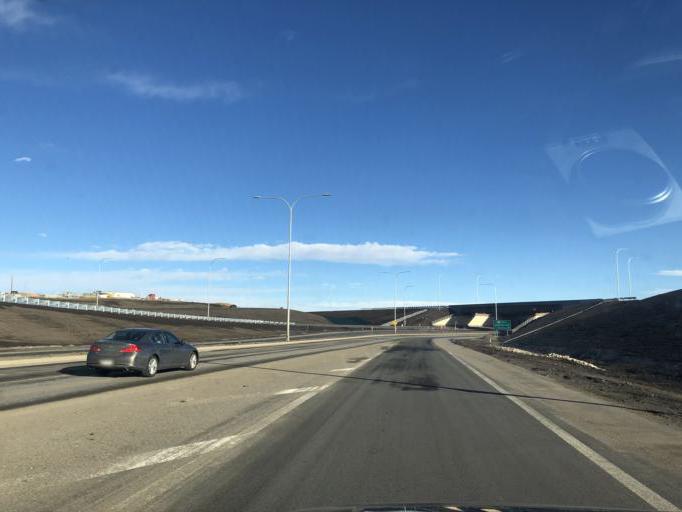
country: CA
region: Alberta
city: Calgary
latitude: 50.9499
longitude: -114.1435
